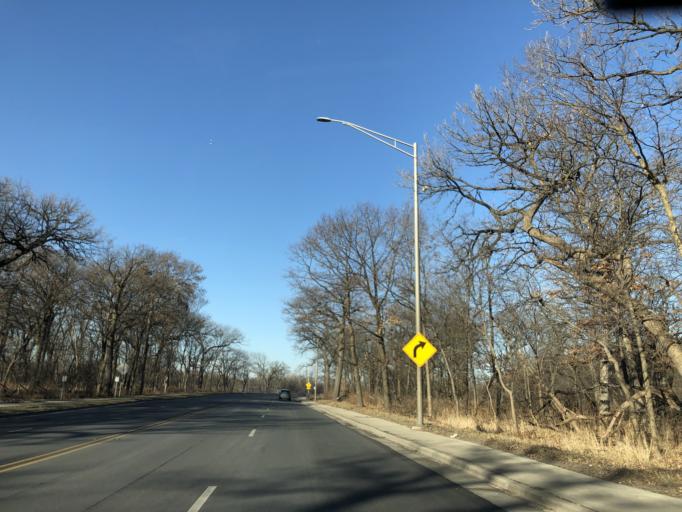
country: US
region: Illinois
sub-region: Cook County
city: Riverside
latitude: 41.8368
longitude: -87.8304
